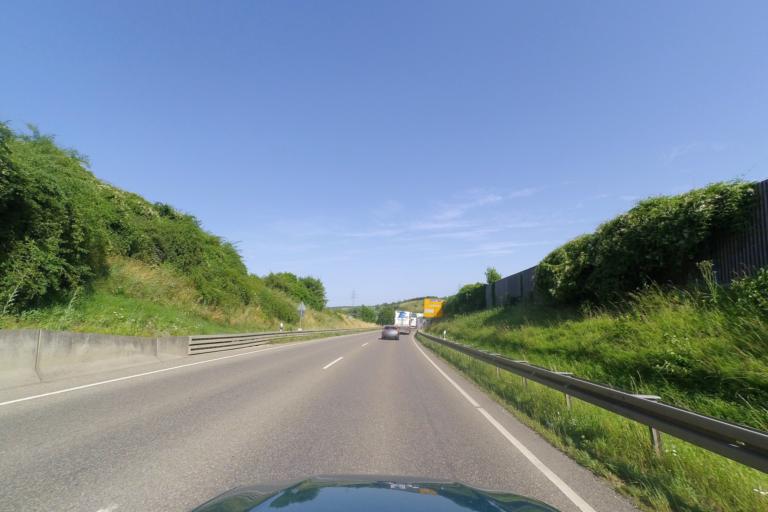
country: DE
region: Baden-Wuerttemberg
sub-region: Regierungsbezirk Stuttgart
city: Herbrechtingen
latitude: 48.6285
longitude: 10.1828
